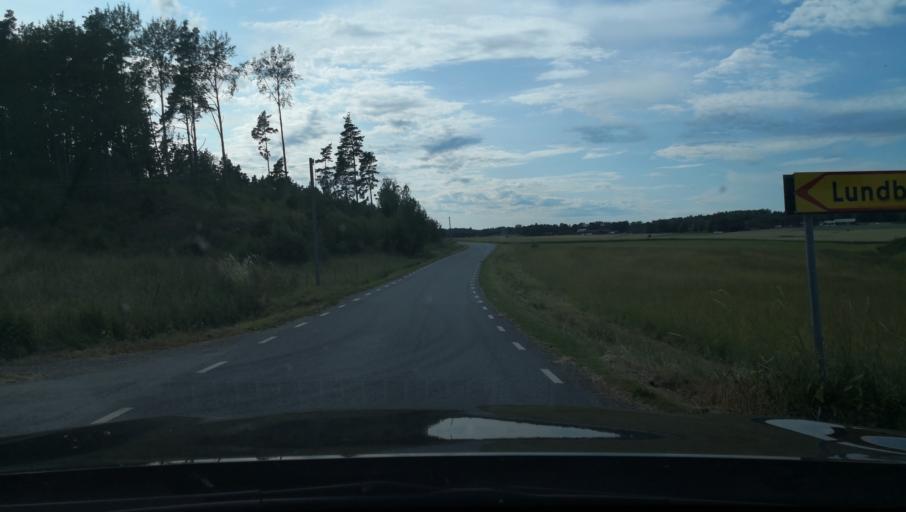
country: SE
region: Uppsala
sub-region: Enkopings Kommun
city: Orsundsbro
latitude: 59.6915
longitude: 17.3585
